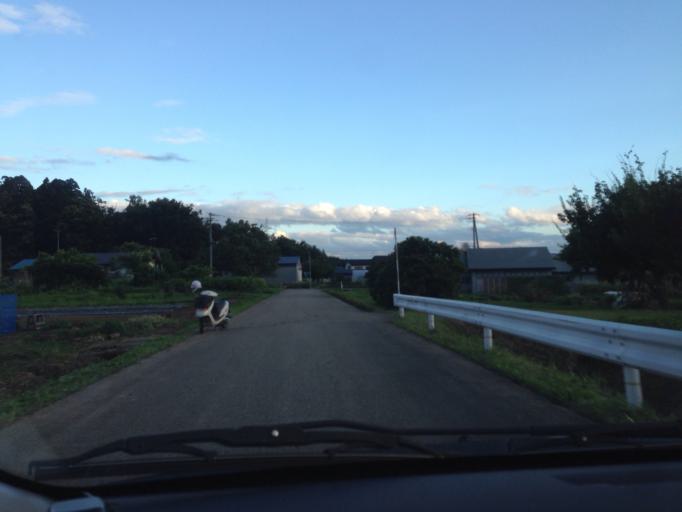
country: JP
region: Fukushima
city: Kitakata
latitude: 37.6985
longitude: 139.8598
